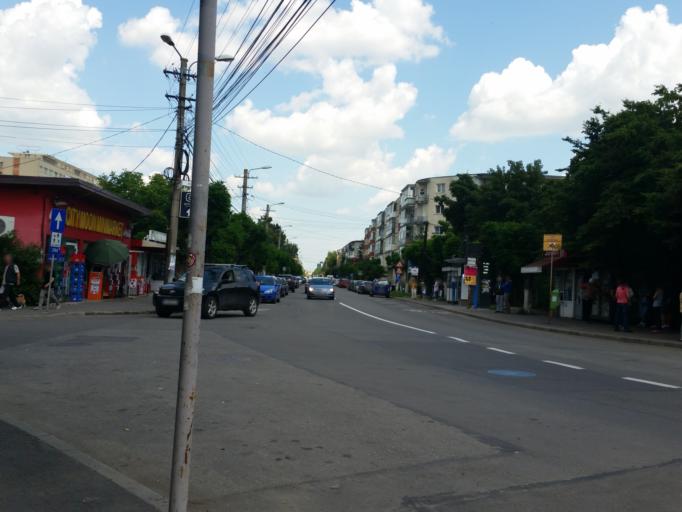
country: RO
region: Cluj
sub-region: Municipiul Cluj-Napoca
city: Cluj-Napoca
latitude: 46.7697
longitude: 23.5551
